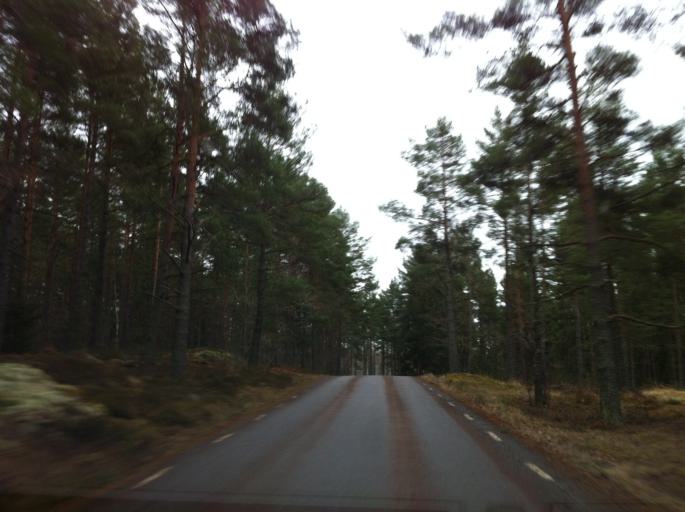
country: SE
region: Kalmar
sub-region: Vasterviks Kommun
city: Forserum
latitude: 57.9280
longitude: 16.5304
